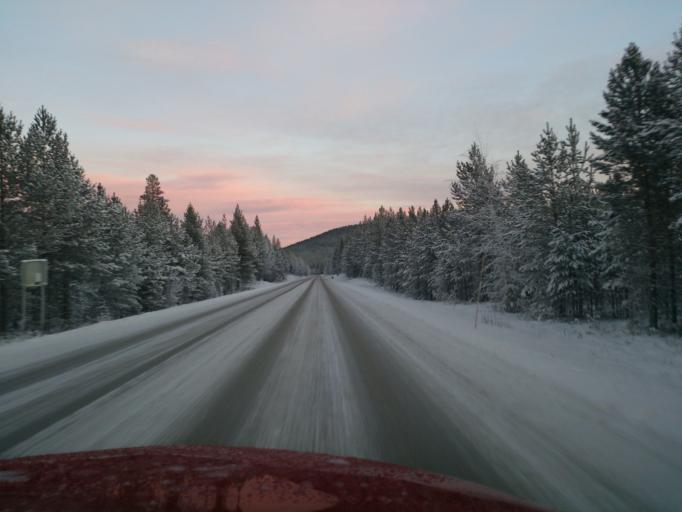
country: SE
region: Jaemtland
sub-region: Harjedalens Kommun
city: Sveg
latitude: 62.4082
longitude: 13.7476
